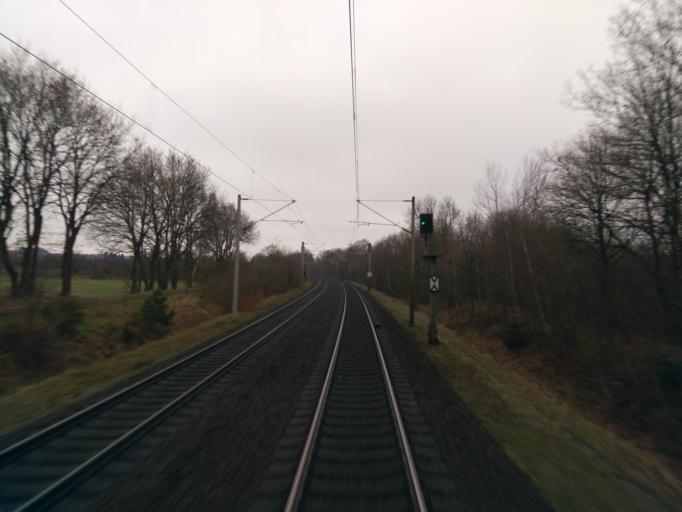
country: DE
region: Lower Saxony
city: Bendestorf
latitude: 53.3596
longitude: 9.9252
